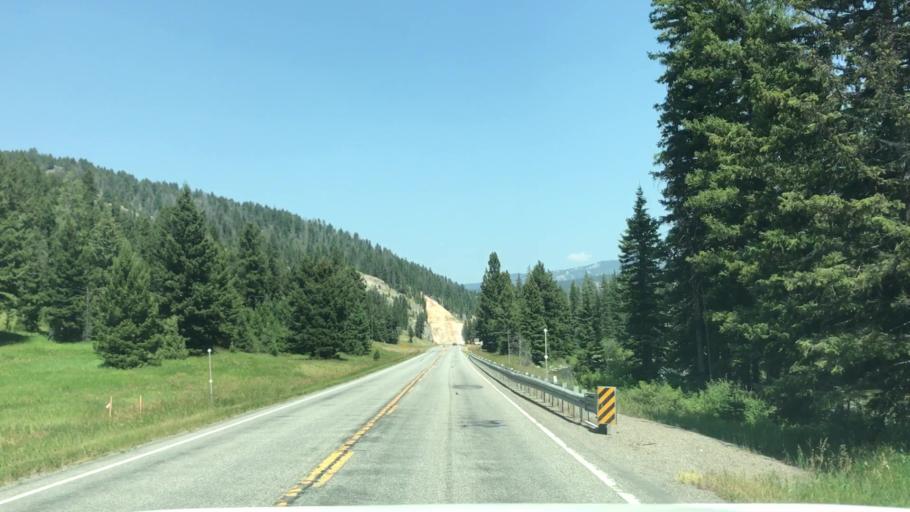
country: US
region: Montana
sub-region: Gallatin County
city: Big Sky
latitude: 45.1707
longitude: -111.2437
